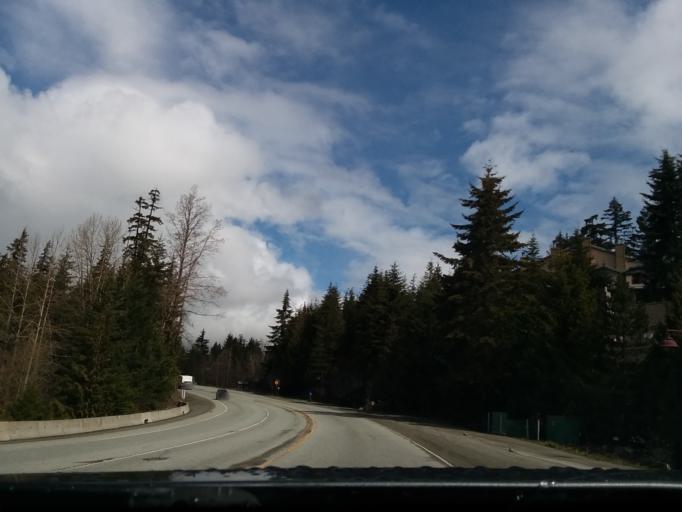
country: CA
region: British Columbia
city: Whistler
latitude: 50.0967
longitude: -122.9901
